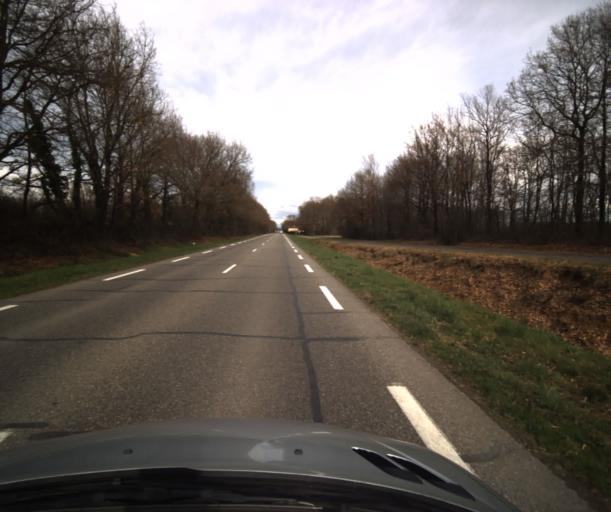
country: FR
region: Midi-Pyrenees
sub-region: Departement du Tarn-et-Garonne
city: Saint-Etienne-de-Tulmont
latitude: 44.0534
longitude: 1.4684
